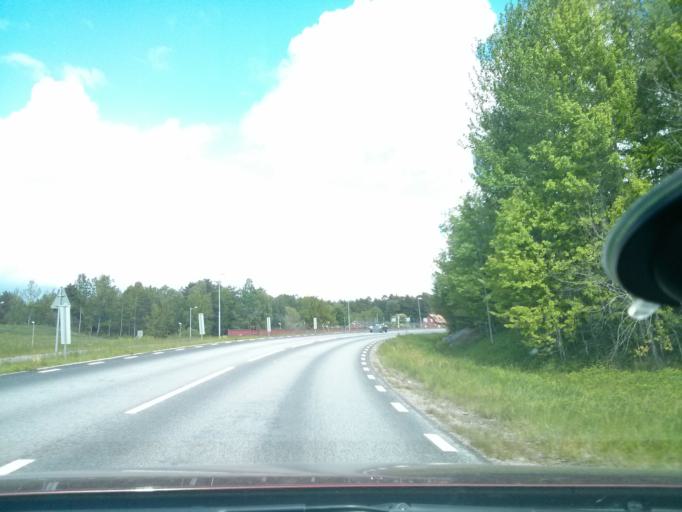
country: SE
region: Soedermanland
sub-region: Nykopings Kommun
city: Nykoping
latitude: 58.7733
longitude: 17.0332
